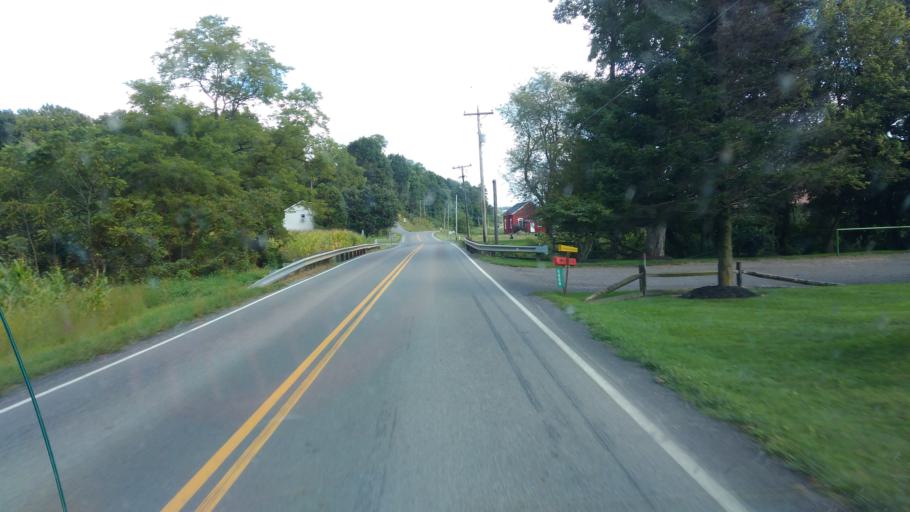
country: US
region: Ohio
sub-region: Holmes County
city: Millersburg
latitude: 40.6152
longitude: -81.8691
